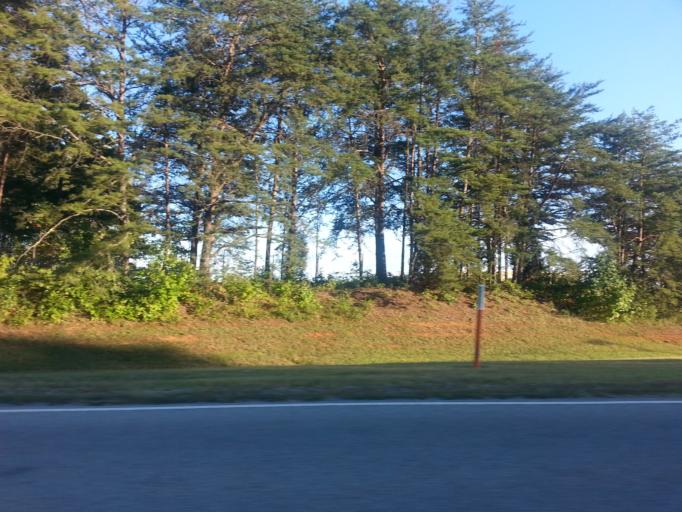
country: US
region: Tennessee
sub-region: Blount County
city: Alcoa
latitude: 35.8228
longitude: -83.9931
